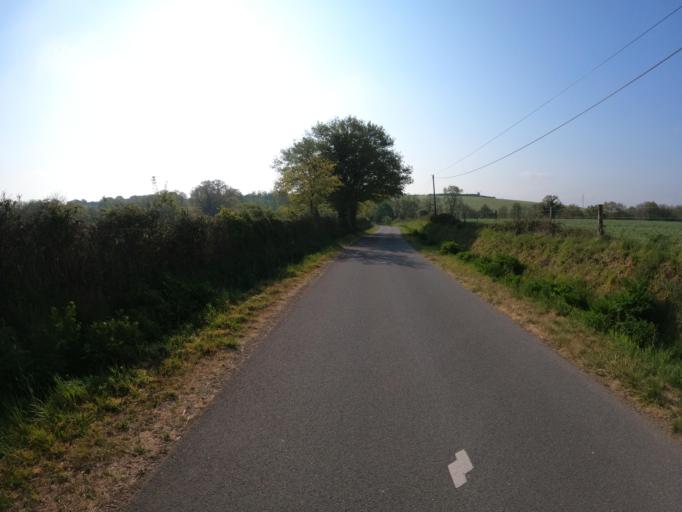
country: FR
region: Pays de la Loire
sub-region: Departement de Maine-et-Loire
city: La Seguiniere
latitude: 47.0691
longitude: -0.9617
